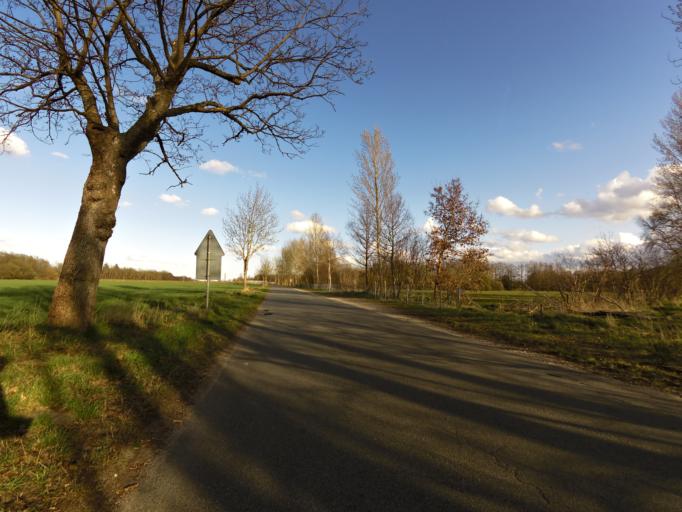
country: DK
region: Capital Region
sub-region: Fredensborg Kommune
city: Niva
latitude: 55.9278
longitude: 12.4967
